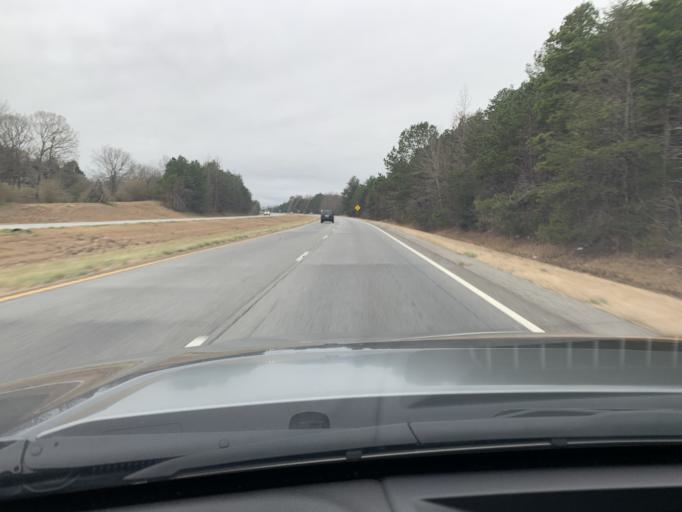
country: US
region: Georgia
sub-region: Habersham County
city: Mount Airy
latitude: 34.5729
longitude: -83.4710
